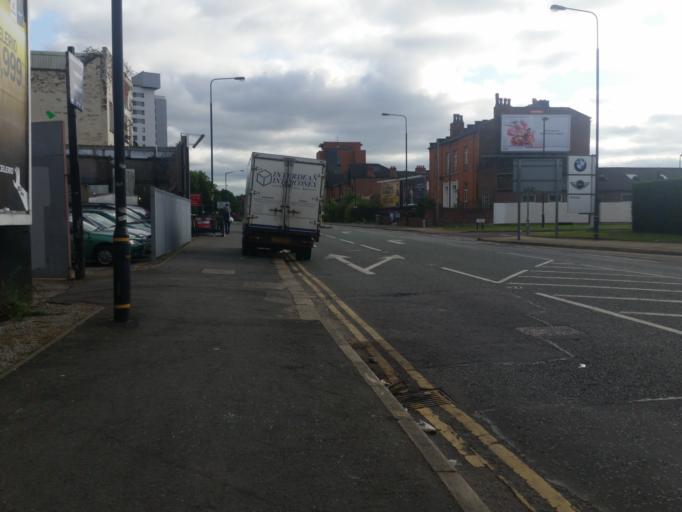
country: GB
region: England
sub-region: Manchester
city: Hulme
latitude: 53.4688
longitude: -2.2661
